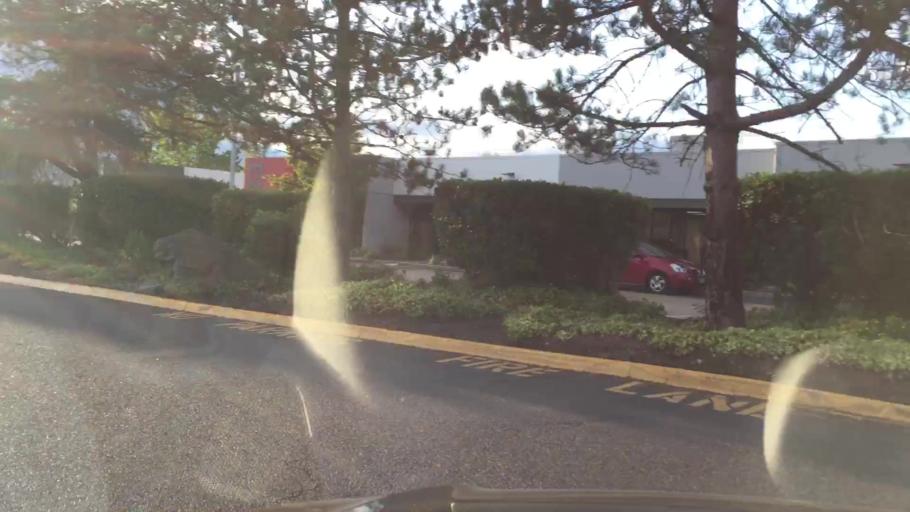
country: US
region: Washington
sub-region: King County
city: Tukwila
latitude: 47.4466
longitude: -122.2473
